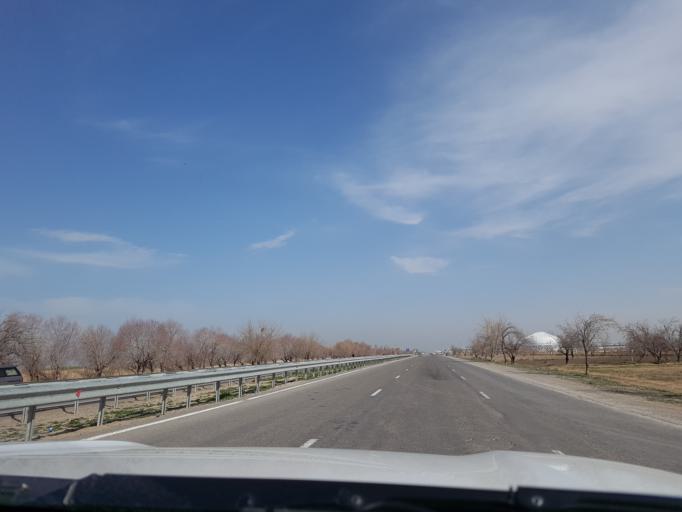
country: TM
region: Mary
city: Mary
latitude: 37.5066
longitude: 61.7126
